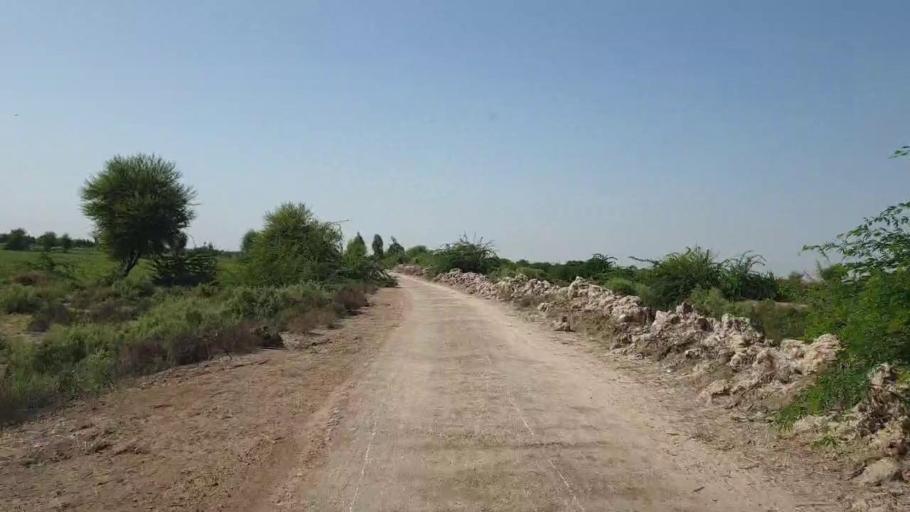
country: PK
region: Sindh
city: Tando Bago
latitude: 24.7062
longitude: 69.0526
